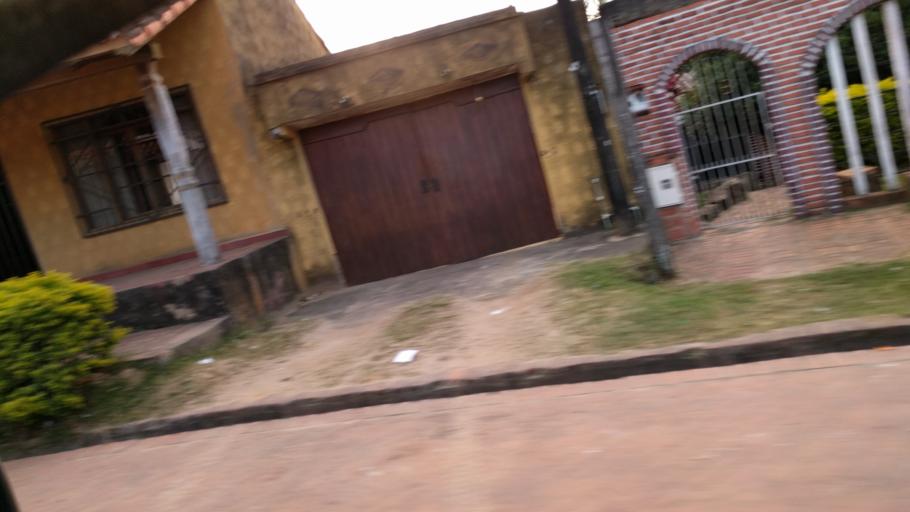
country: BO
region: Santa Cruz
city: Buena Vista
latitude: -17.4585
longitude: -63.6597
